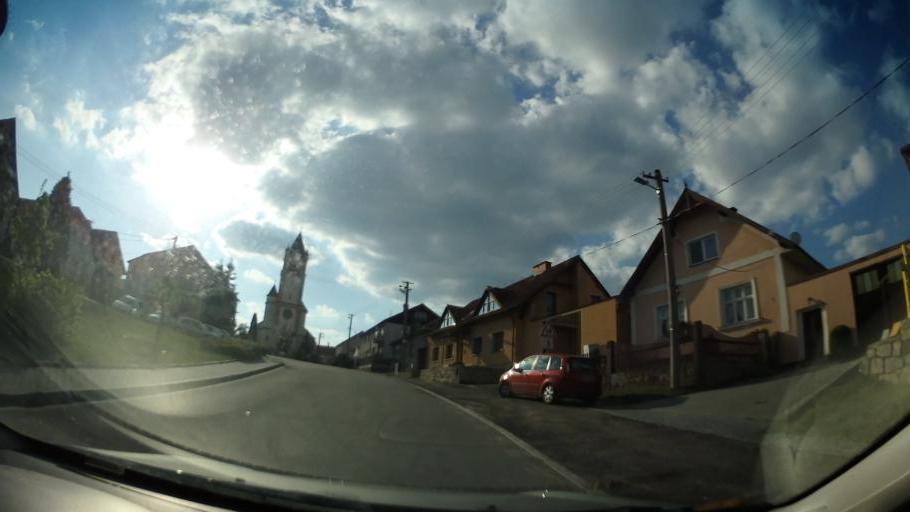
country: CZ
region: Vysocina
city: Merin
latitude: 49.3496
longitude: 15.9390
